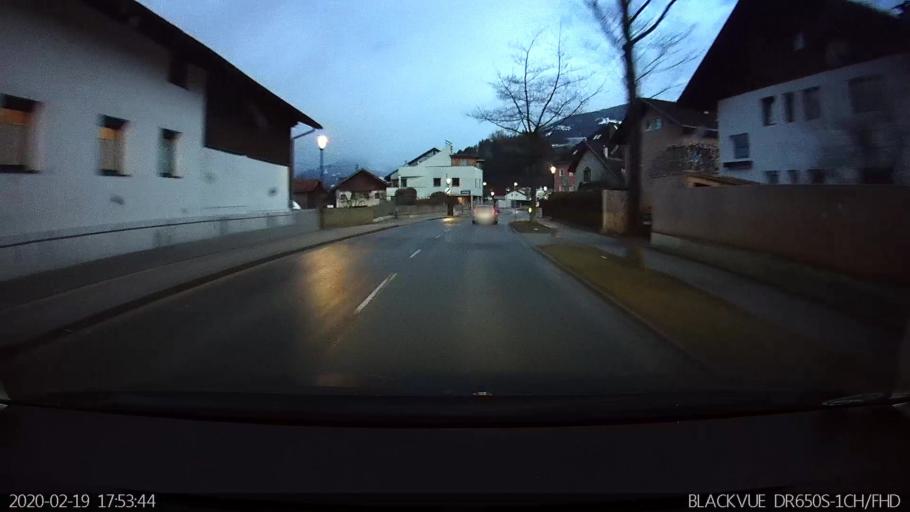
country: AT
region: Tyrol
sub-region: Politischer Bezirk Innsbruck Land
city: Volders
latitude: 47.2881
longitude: 11.5689
